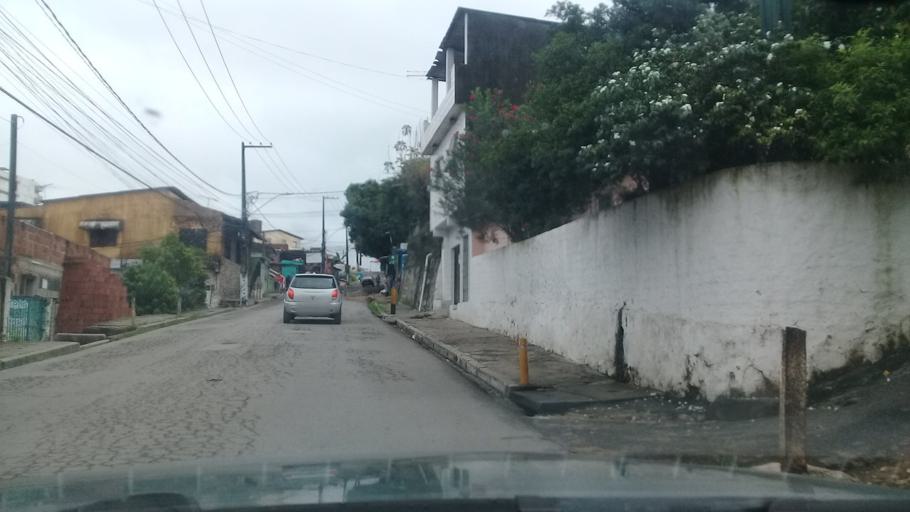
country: BR
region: Pernambuco
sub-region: Jaboatao Dos Guararapes
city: Jaboatao dos Guararapes
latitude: -8.0897
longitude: -34.9739
